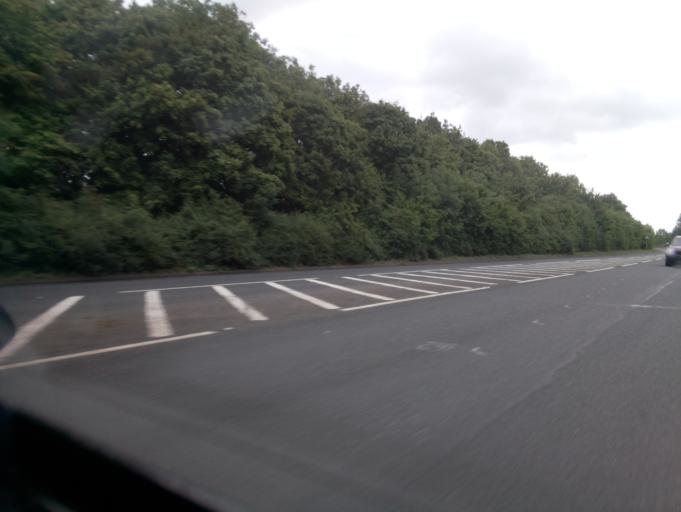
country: GB
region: England
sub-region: Worcestershire
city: Droitwich
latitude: 52.2588
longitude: -2.1753
